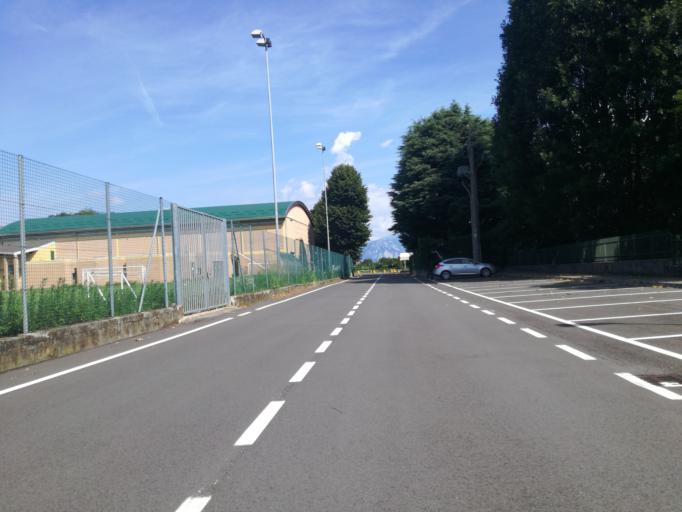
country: IT
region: Lombardy
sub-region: Provincia di Lecco
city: Imbersago
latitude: 45.7057
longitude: 9.4519
